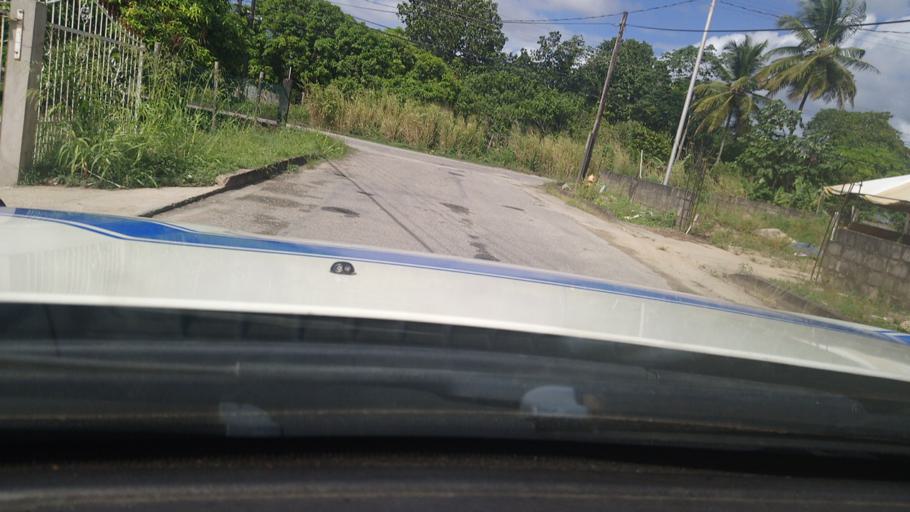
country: TT
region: Borough of Arima
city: Arima
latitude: 10.6181
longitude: -61.2996
